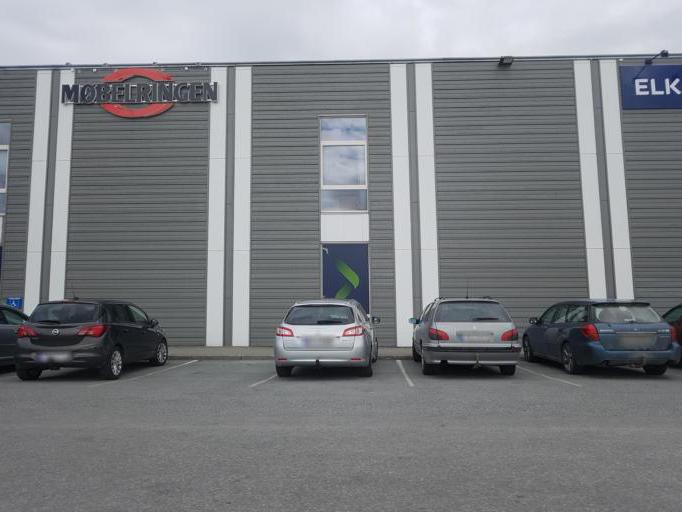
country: NO
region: Nord-Trondelag
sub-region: Levanger
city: Levanger
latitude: 63.7344
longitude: 11.2827
